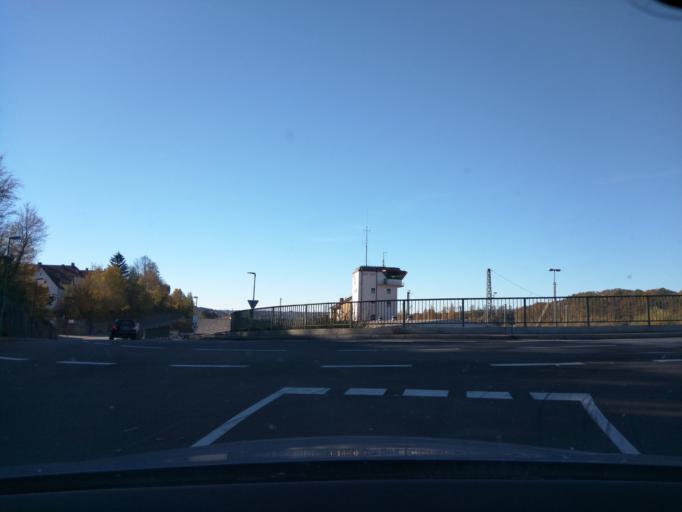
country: DE
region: Bavaria
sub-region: Lower Bavaria
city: Passau
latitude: 48.5724
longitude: 13.4386
